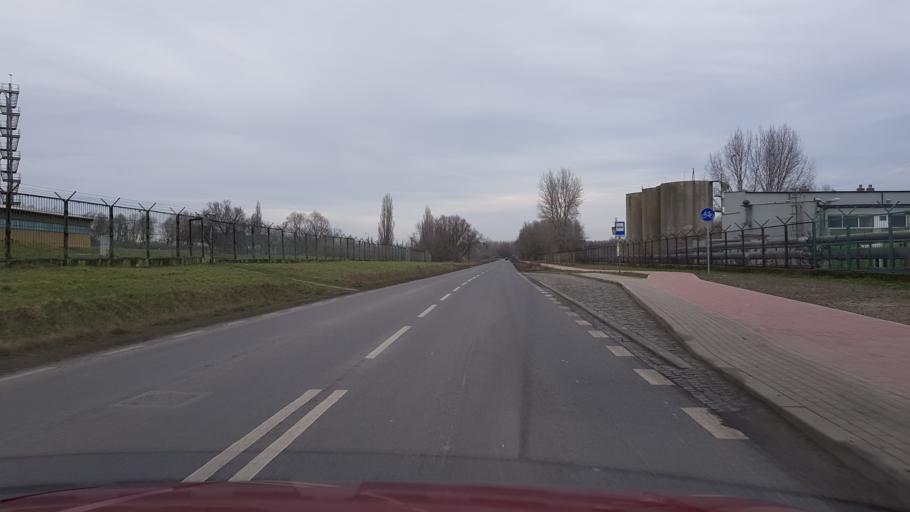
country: PL
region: West Pomeranian Voivodeship
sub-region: Powiat policki
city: Police
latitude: 53.5783
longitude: 14.5542
